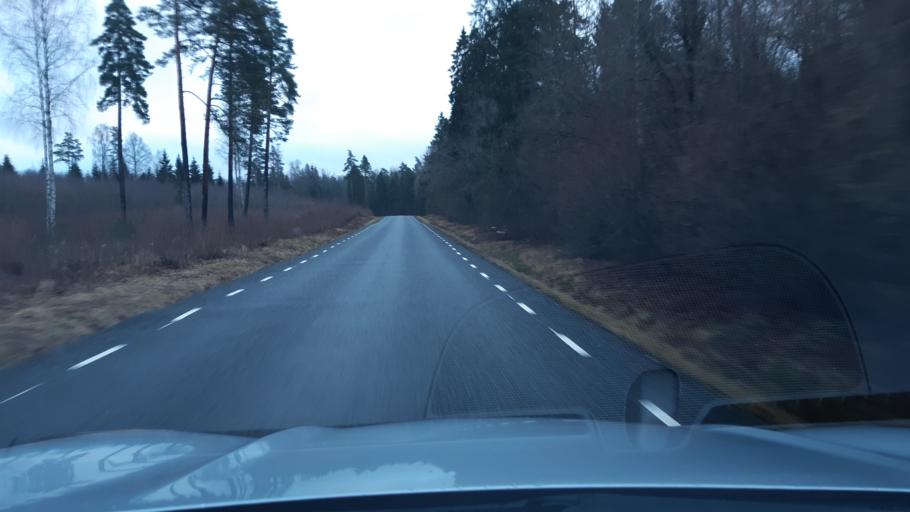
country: EE
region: Harju
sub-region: Saku vald
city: Saku
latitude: 59.1812
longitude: 24.6114
